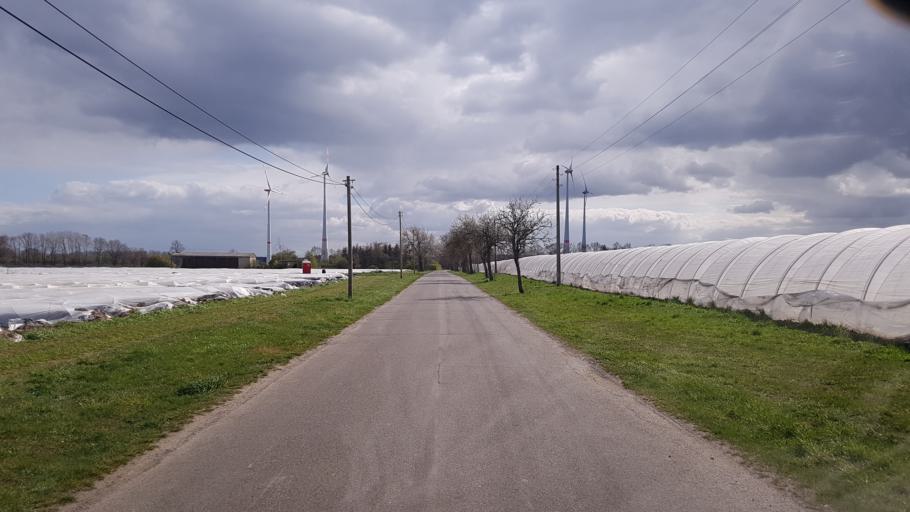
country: DE
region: Brandenburg
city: Calau
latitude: 51.7482
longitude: 14.0029
